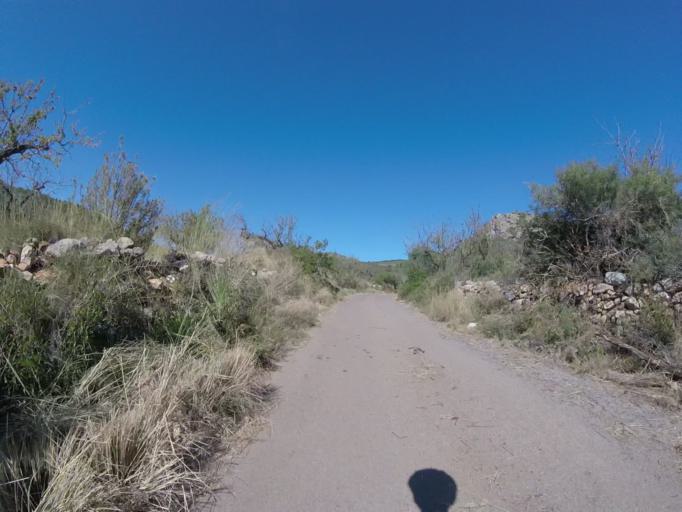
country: ES
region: Valencia
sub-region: Provincia de Castello
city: Orpesa/Oropesa del Mar
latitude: 40.1355
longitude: 0.1051
